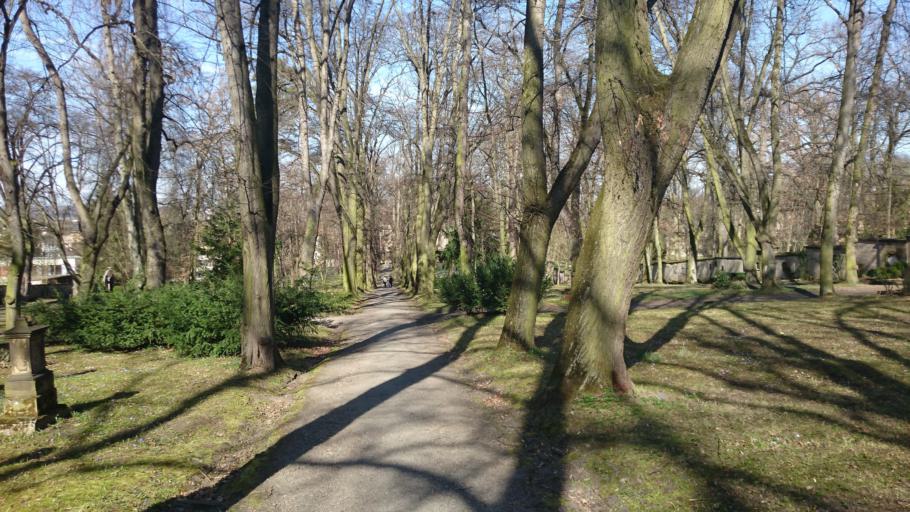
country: DE
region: Thuringia
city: Weimar
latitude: 50.9727
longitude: 11.3244
